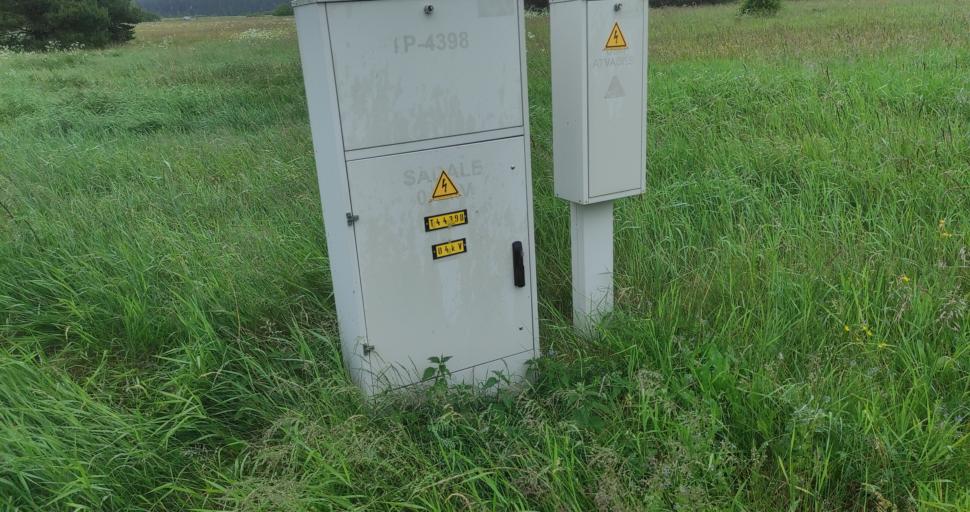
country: LV
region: Pavilostas
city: Pavilosta
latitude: 56.9564
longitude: 21.3149
